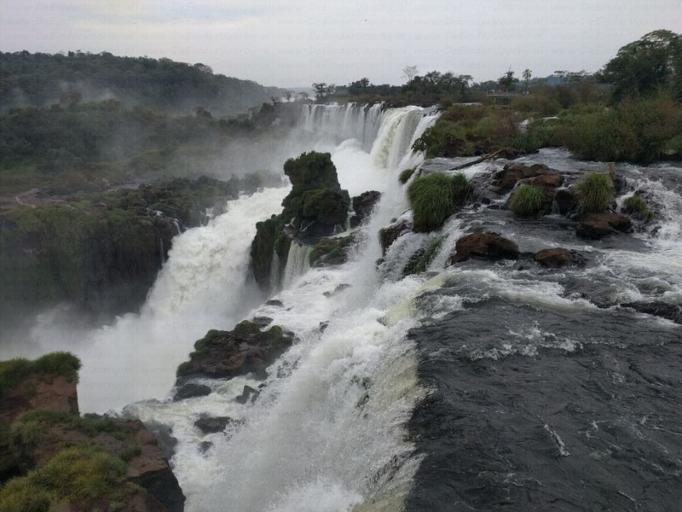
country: AR
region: Misiones
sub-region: Departamento de Iguazu
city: Puerto Iguazu
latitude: -25.6875
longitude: -54.4454
